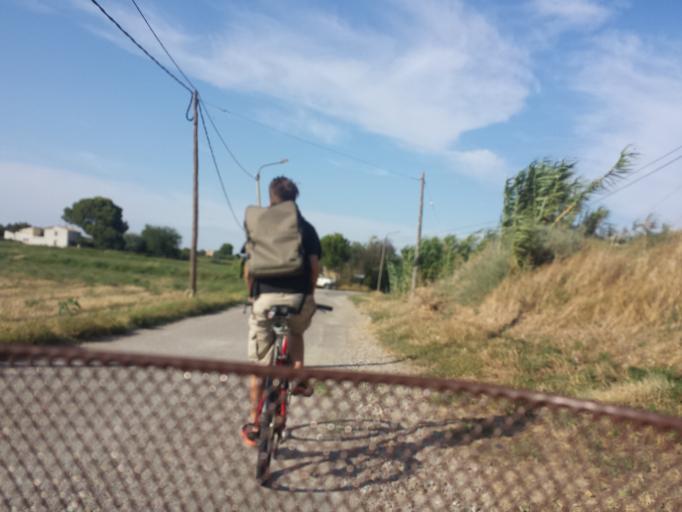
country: ES
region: Aragon
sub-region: Provincia de Zaragoza
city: Zaragoza
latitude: 41.6949
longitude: -0.8615
